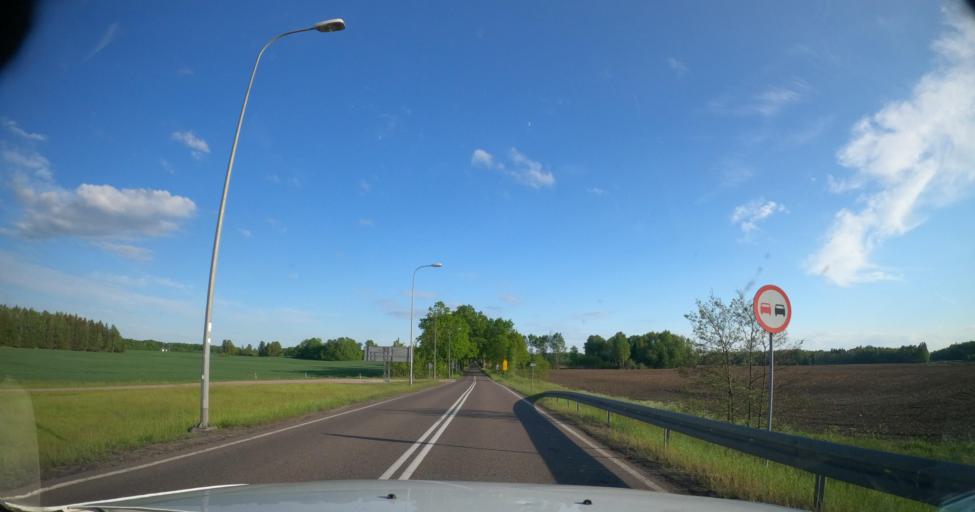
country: PL
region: Warmian-Masurian Voivodeship
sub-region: Powiat braniewski
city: Braniewo
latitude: 54.2869
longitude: 19.7914
